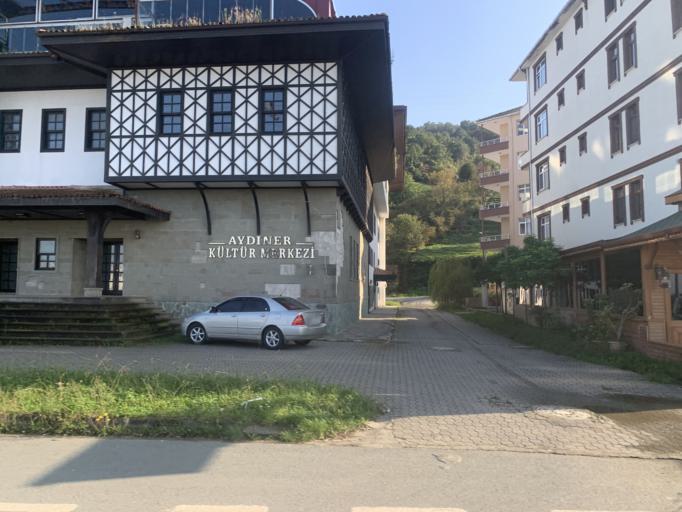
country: TR
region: Trabzon
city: Of
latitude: 40.9381
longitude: 40.2533
